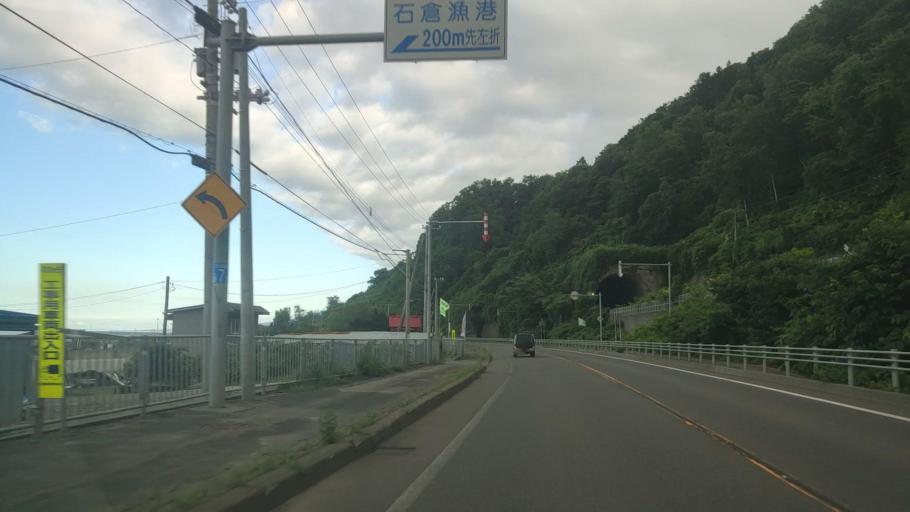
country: JP
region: Hokkaido
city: Nanae
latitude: 42.1575
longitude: 140.4753
